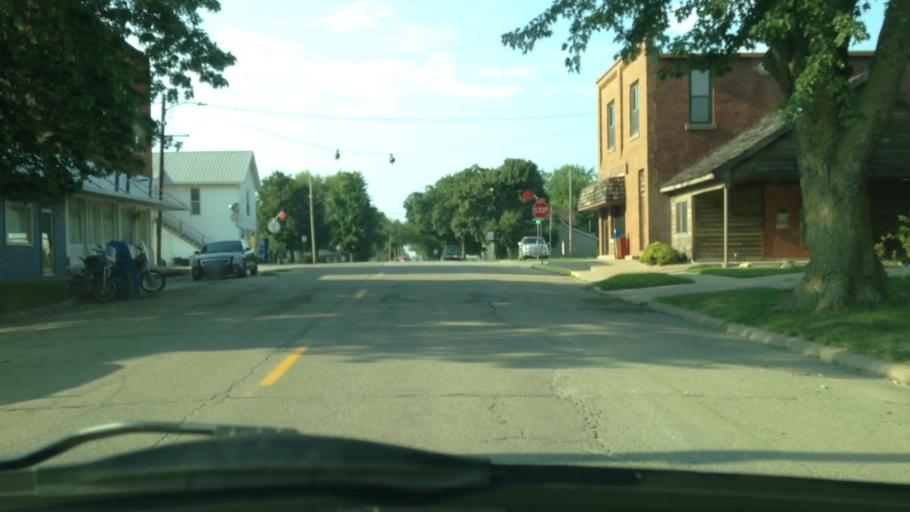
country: US
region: Iowa
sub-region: Henry County
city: Winfield
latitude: 41.2135
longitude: -91.5388
